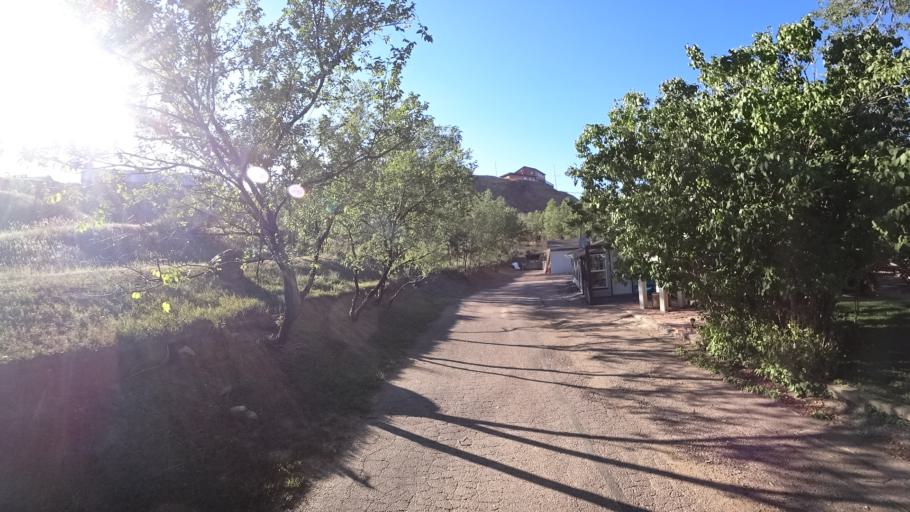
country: US
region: Colorado
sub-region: El Paso County
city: Manitou Springs
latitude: 38.8330
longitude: -104.8750
